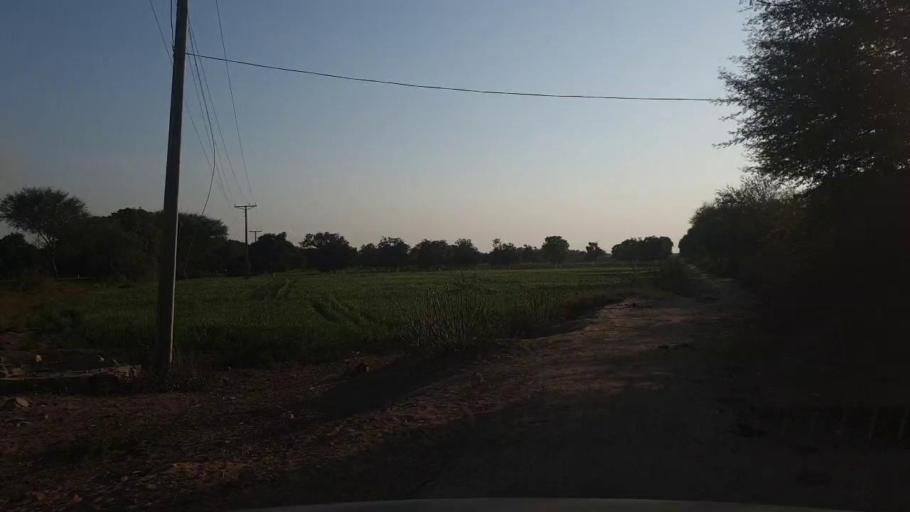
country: PK
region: Sindh
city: Chambar
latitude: 25.2763
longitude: 68.8774
